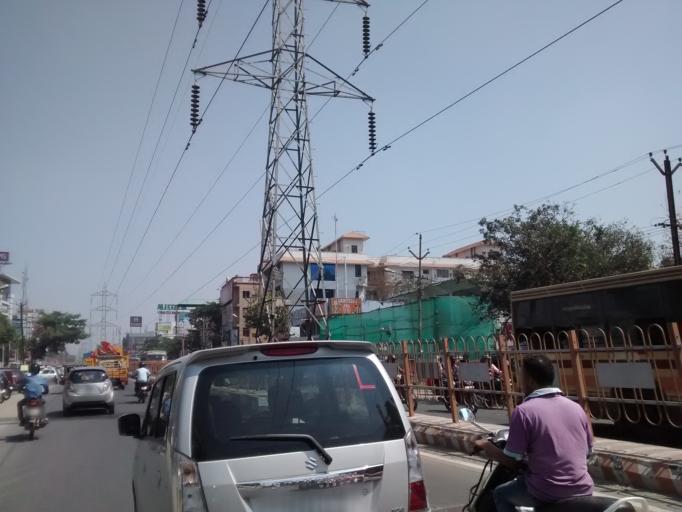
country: IN
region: Tamil Nadu
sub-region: Coimbatore
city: Coimbatore
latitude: 11.0191
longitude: 76.9612
